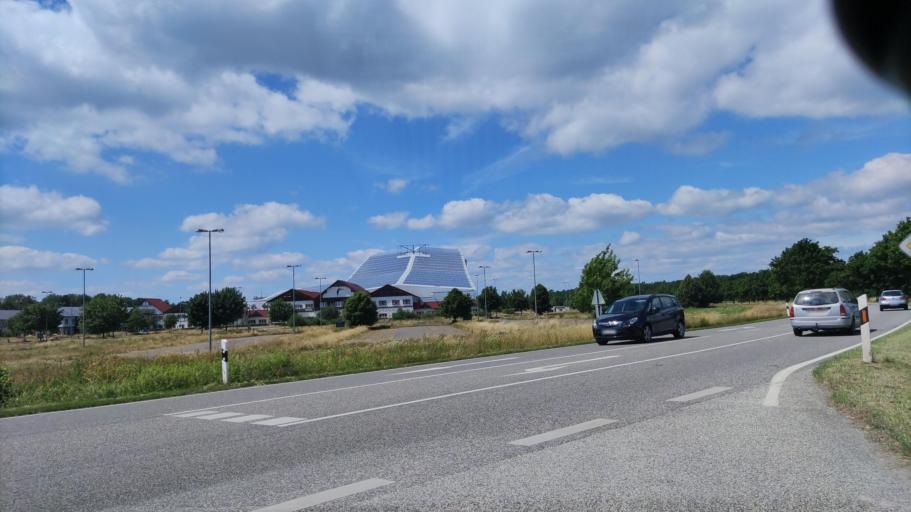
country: DE
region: Mecklenburg-Vorpommern
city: Wittenburg
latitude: 53.5055
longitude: 11.0992
